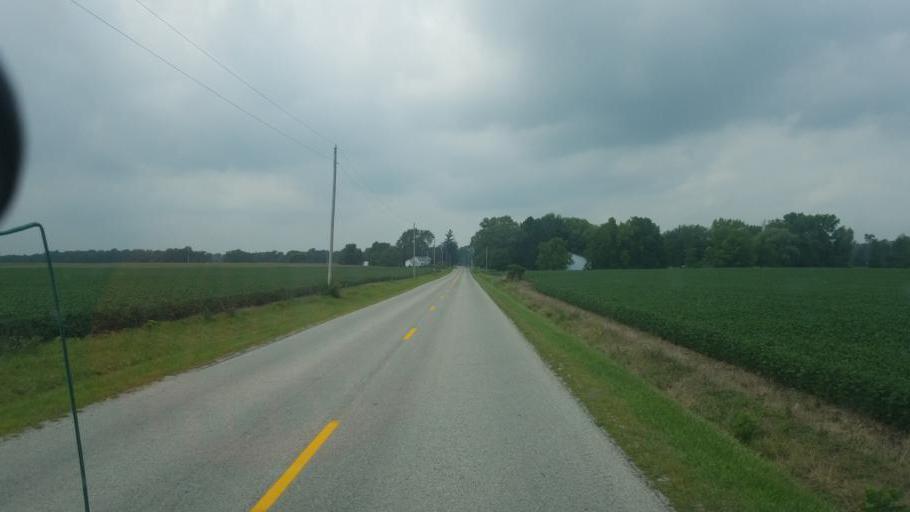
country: US
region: Ohio
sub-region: Huron County
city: Greenwich
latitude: 41.0786
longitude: -82.5589
